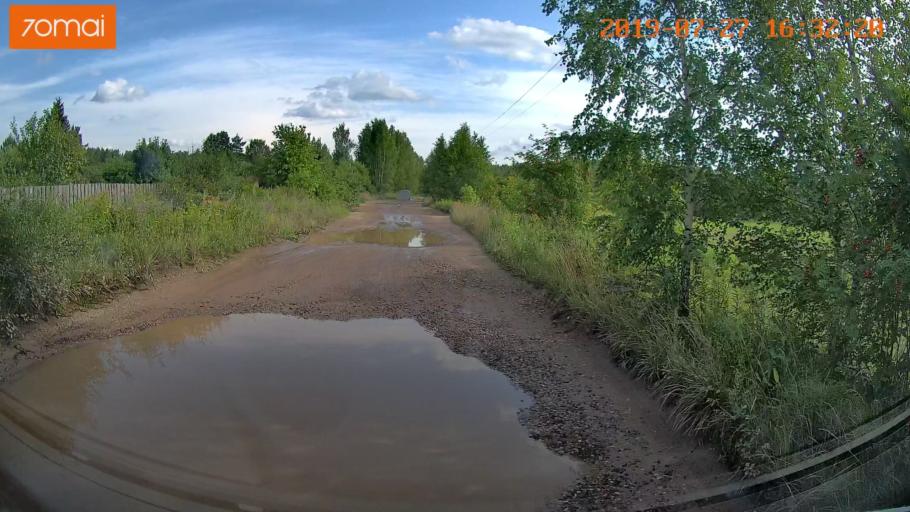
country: RU
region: Ivanovo
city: Novo-Talitsy
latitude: 57.0899
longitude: 40.8515
